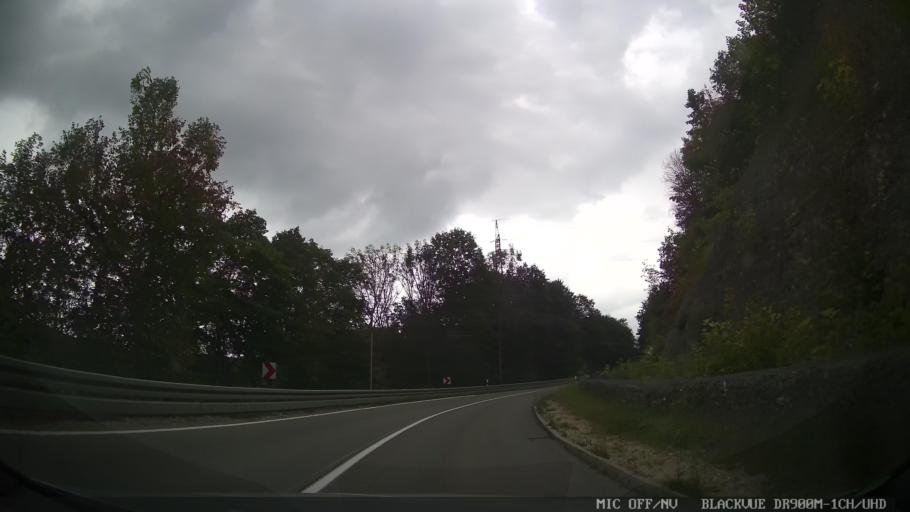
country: DE
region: Baden-Wuerttemberg
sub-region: Freiburg Region
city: Fridingen an der Donau
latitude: 48.0113
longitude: 8.9161
